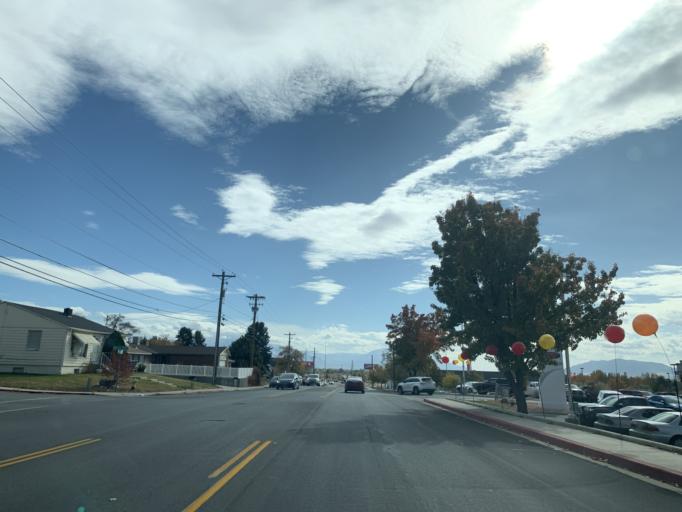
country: US
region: Utah
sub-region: Utah County
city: Orem
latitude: 40.2710
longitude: -111.7118
